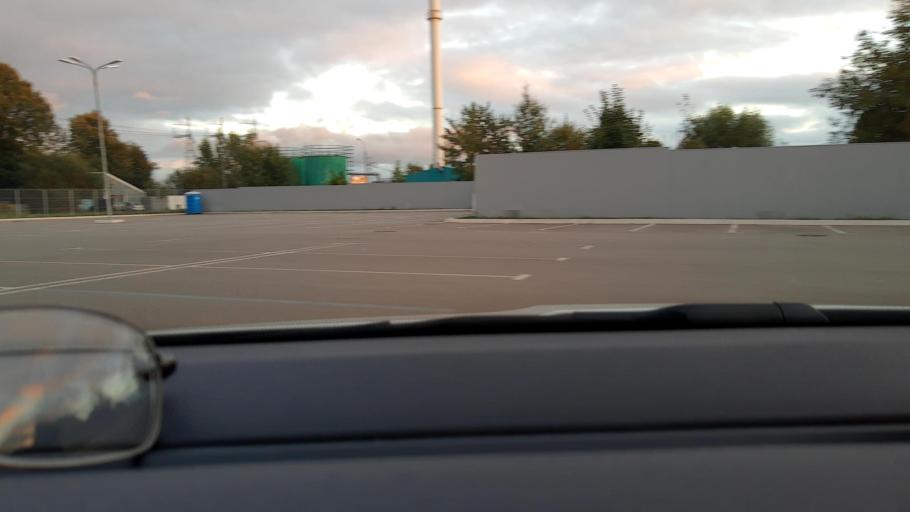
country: RU
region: Moskovskaya
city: Arkhangel'skoye
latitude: 55.8074
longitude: 37.2979
